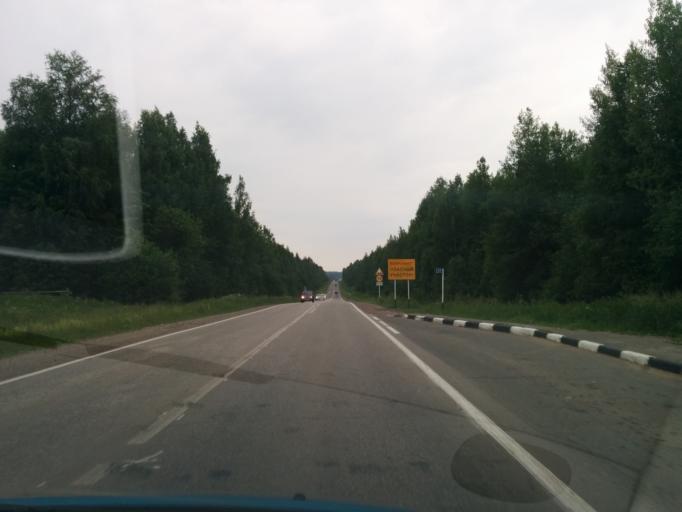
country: RU
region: Perm
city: Perm
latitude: 58.1459
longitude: 56.2624
